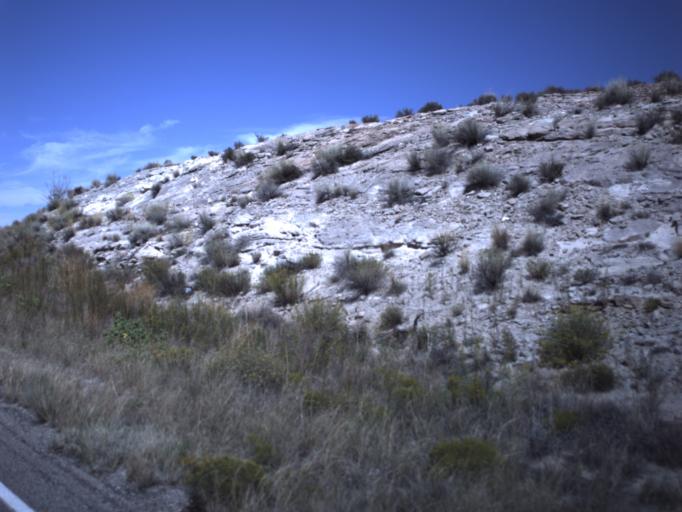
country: US
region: Utah
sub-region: San Juan County
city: Blanding
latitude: 37.2747
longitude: -109.3591
